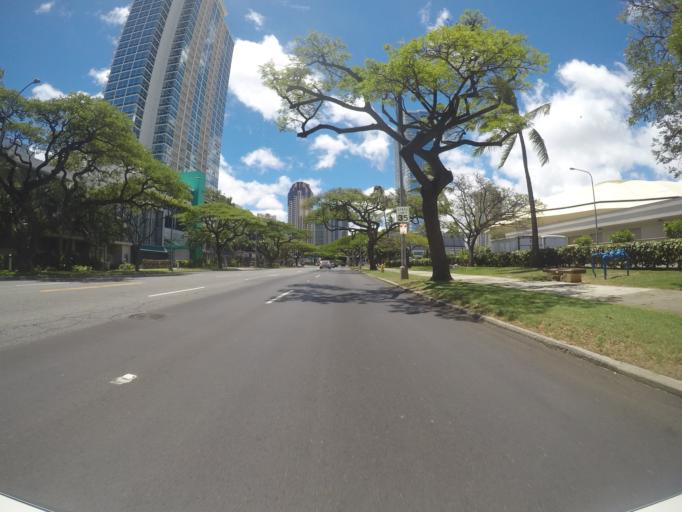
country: US
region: Hawaii
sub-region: Honolulu County
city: Honolulu
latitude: 21.2978
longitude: -157.8517
